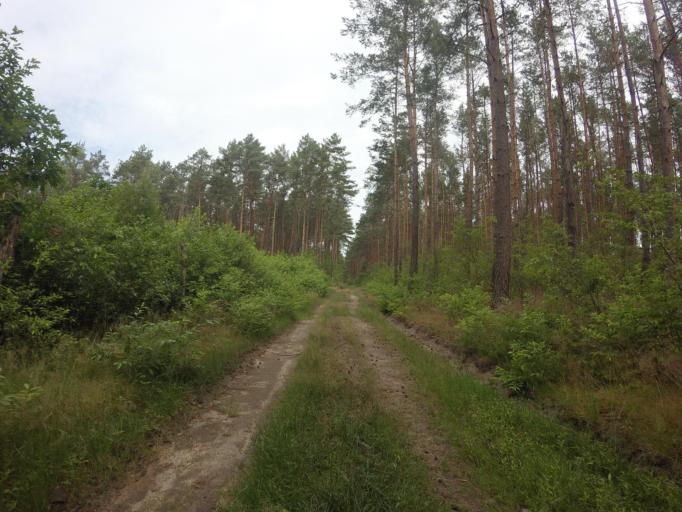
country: PL
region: West Pomeranian Voivodeship
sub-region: Powiat choszczenski
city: Bierzwnik
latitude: 53.1237
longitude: 15.6659
